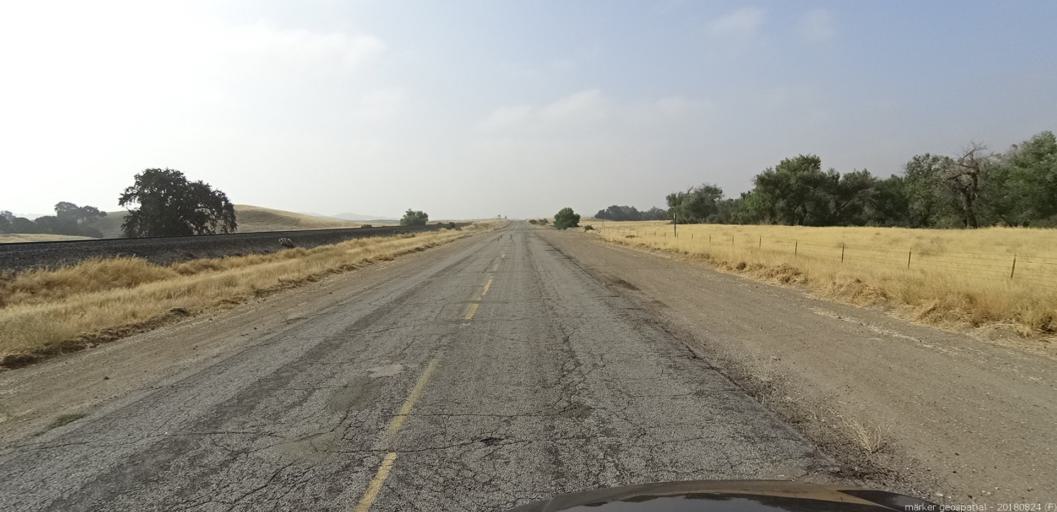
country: US
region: California
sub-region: San Luis Obispo County
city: San Miguel
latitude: 35.8443
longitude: -120.7530
